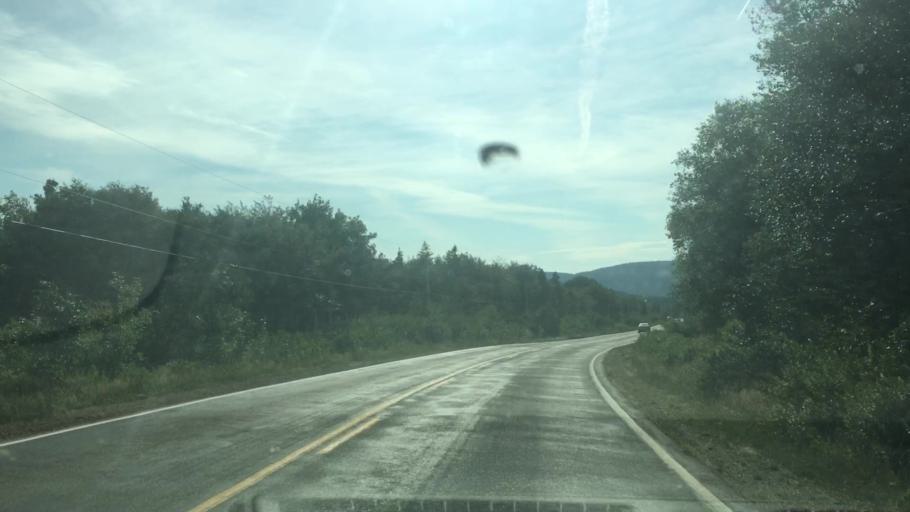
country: CA
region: Nova Scotia
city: Sydney Mines
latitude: 46.8772
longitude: -60.5194
